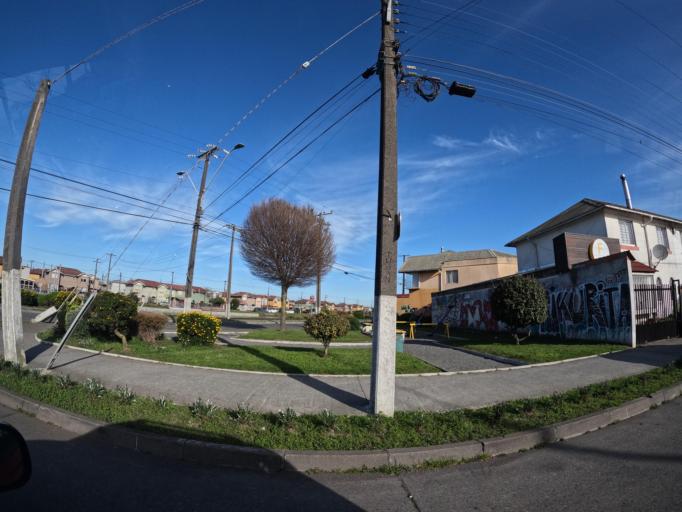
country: CL
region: Biobio
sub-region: Provincia de Concepcion
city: Talcahuano
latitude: -36.7444
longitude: -73.0839
